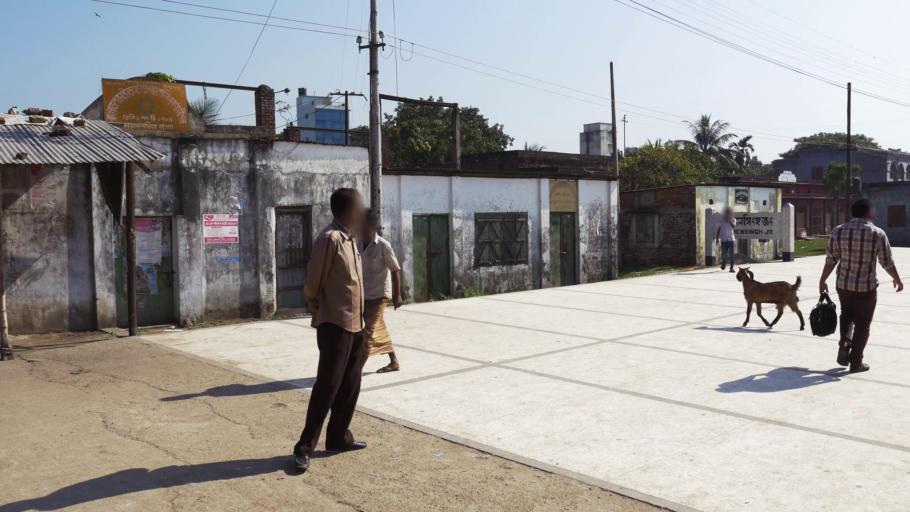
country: BD
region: Dhaka
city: Mymensingh
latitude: 24.6378
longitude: 90.4571
